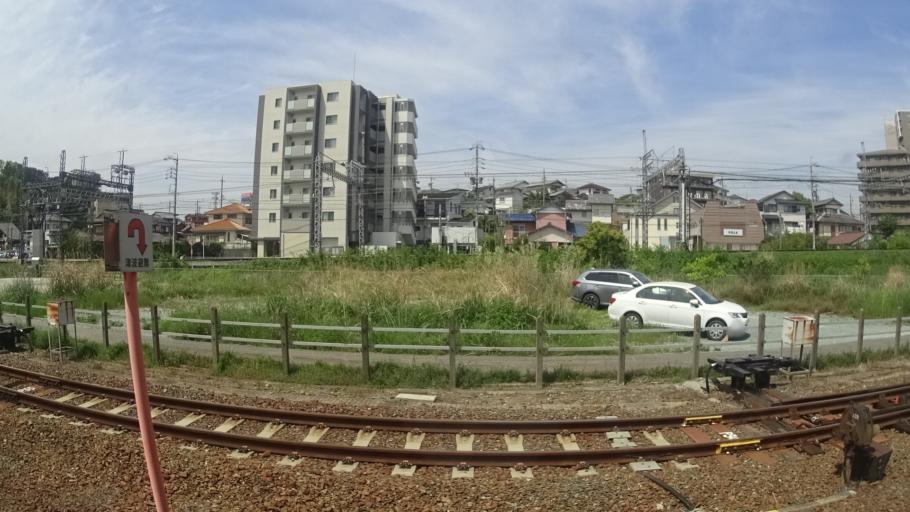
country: JP
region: Mie
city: Tsu-shi
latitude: 34.7362
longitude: 136.5105
